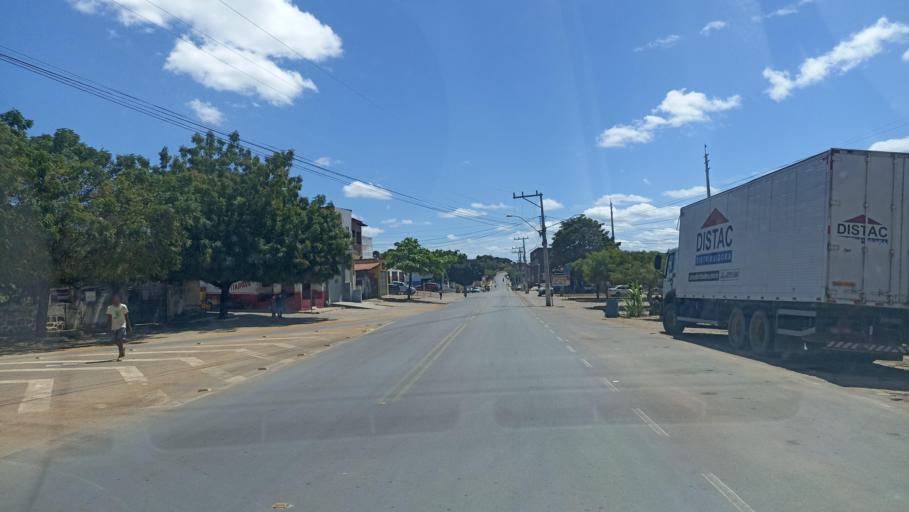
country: BR
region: Bahia
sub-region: Andarai
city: Vera Cruz
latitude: -12.8013
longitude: -41.3258
